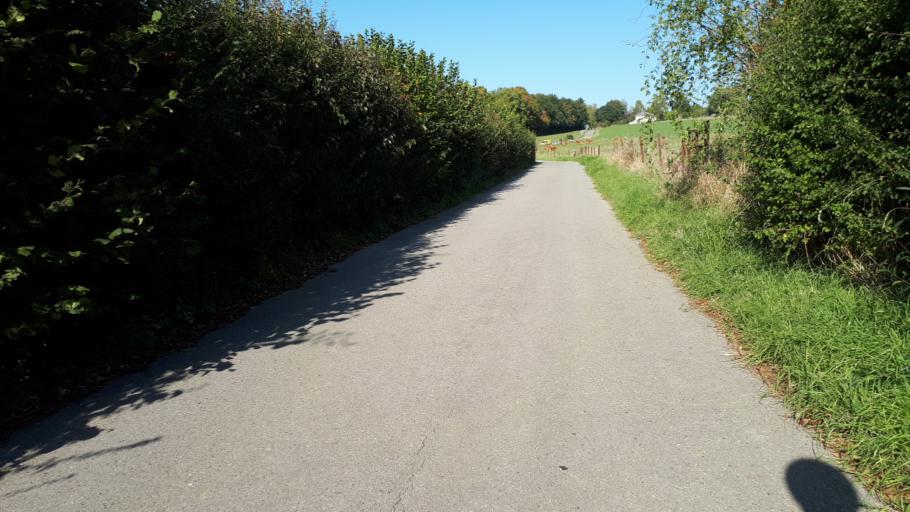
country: LU
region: Luxembourg
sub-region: Canton de Capellen
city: Kehlen
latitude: 49.6593
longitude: 6.0299
